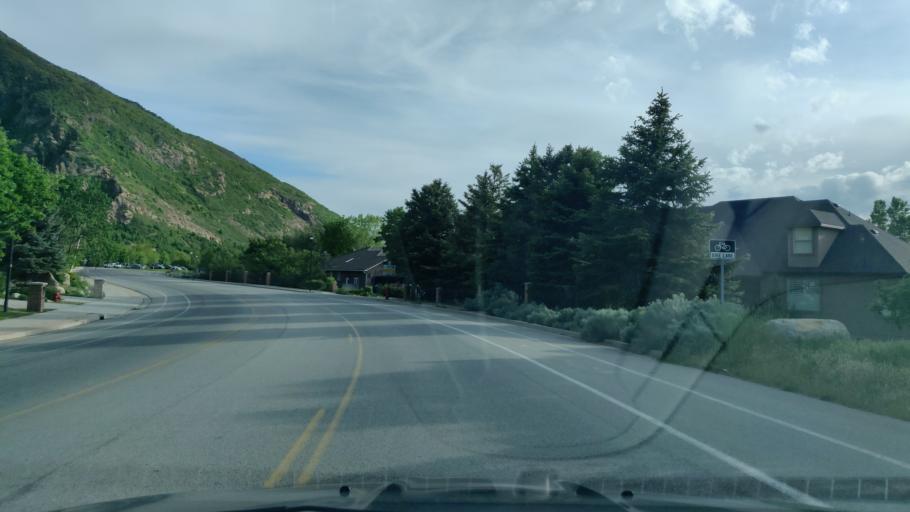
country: US
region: Utah
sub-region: Salt Lake County
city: Granite
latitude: 40.5431
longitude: -111.8127
